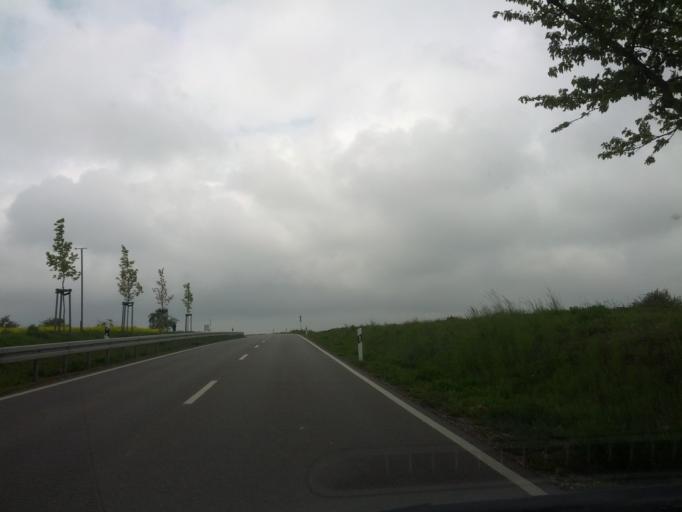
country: DE
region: Baden-Wuerttemberg
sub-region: Regierungsbezirk Stuttgart
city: Magstadt
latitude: 48.7183
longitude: 8.9336
